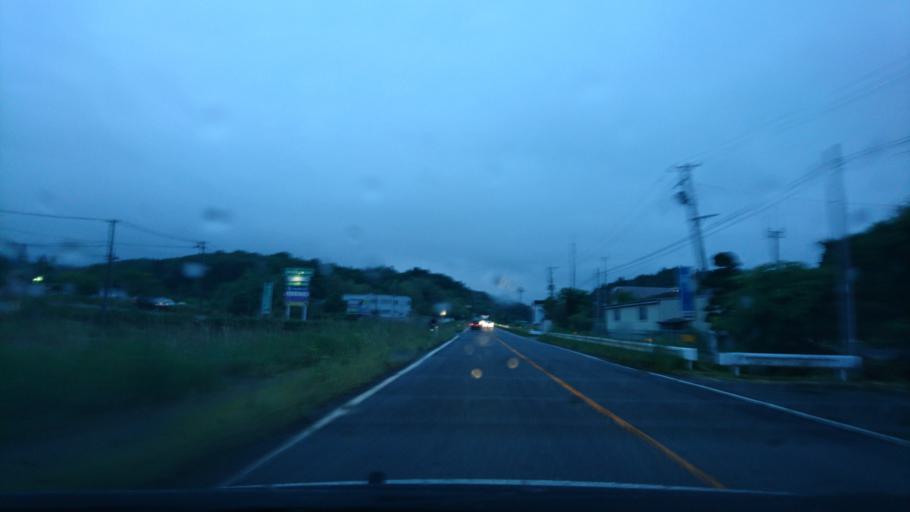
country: JP
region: Iwate
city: Ichinoseki
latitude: 38.7905
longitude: 141.0509
